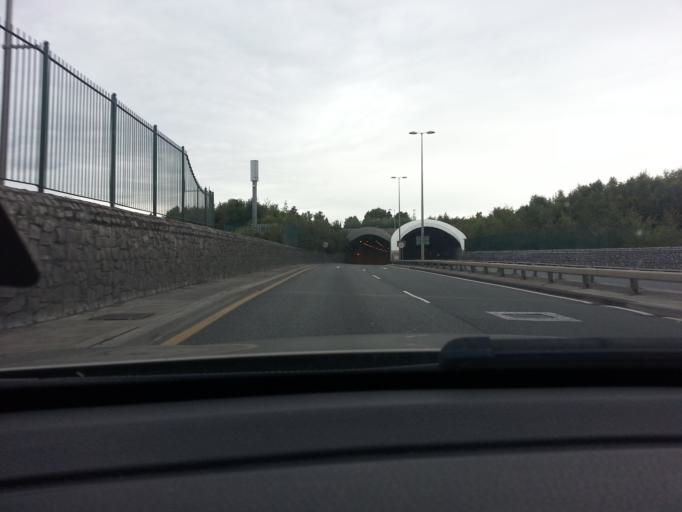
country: IE
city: Fairview
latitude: 53.3575
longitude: -6.2308
